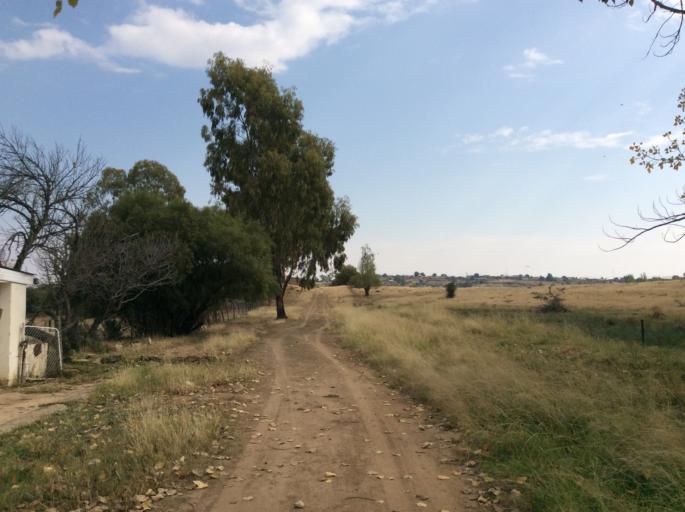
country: LS
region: Mafeteng
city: Mafeteng
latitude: -29.7246
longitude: 27.0432
